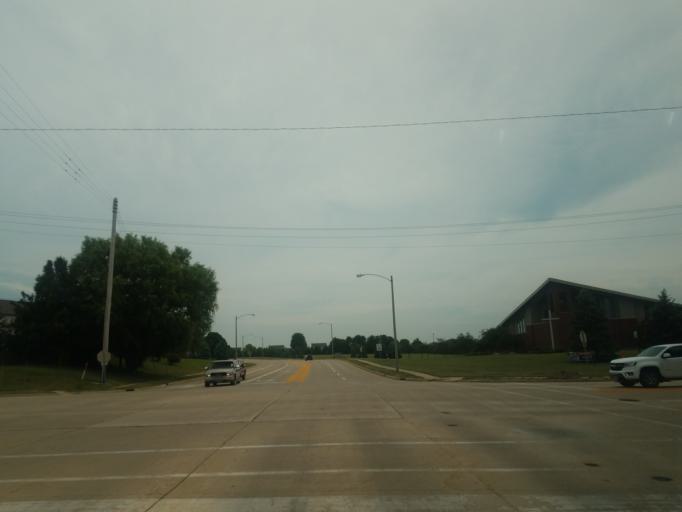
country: US
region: Illinois
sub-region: McLean County
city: Normal
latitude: 40.5179
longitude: -88.9437
